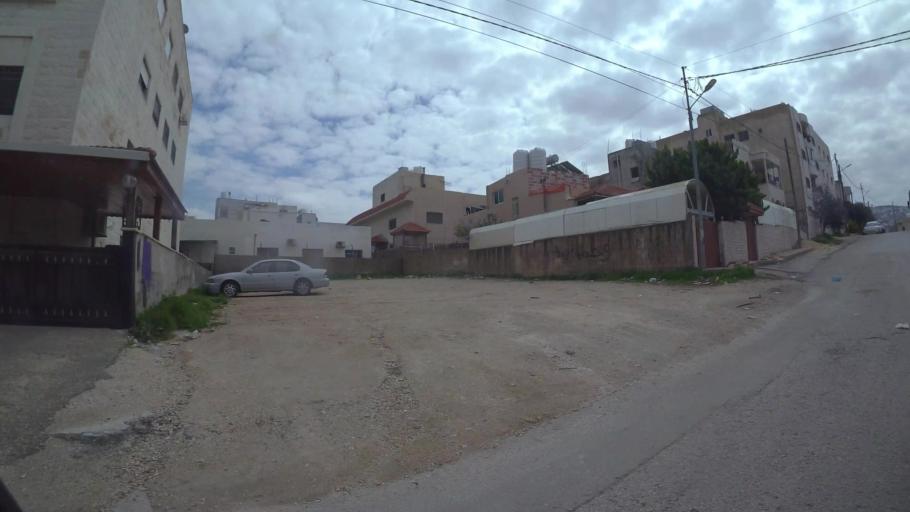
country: JO
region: Amman
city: Al Jubayhah
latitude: 32.0593
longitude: 35.8341
